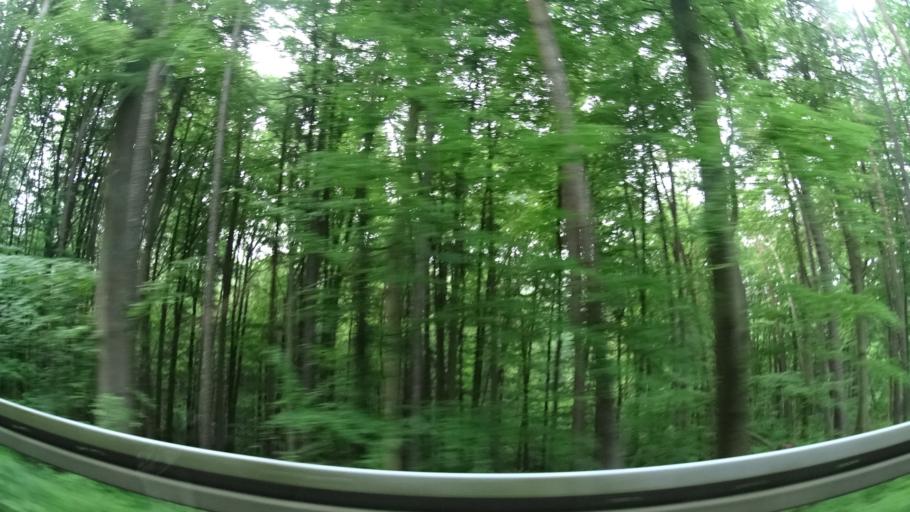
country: DE
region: Bavaria
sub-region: Regierungsbezirk Unterfranken
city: Eschau
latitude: 49.8068
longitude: 9.2231
